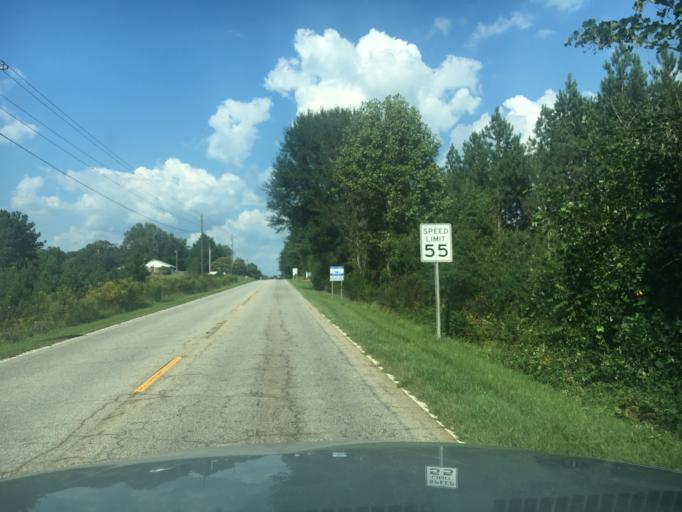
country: US
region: South Carolina
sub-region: Pickens County
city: Liberty
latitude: 34.7287
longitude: -82.6734
